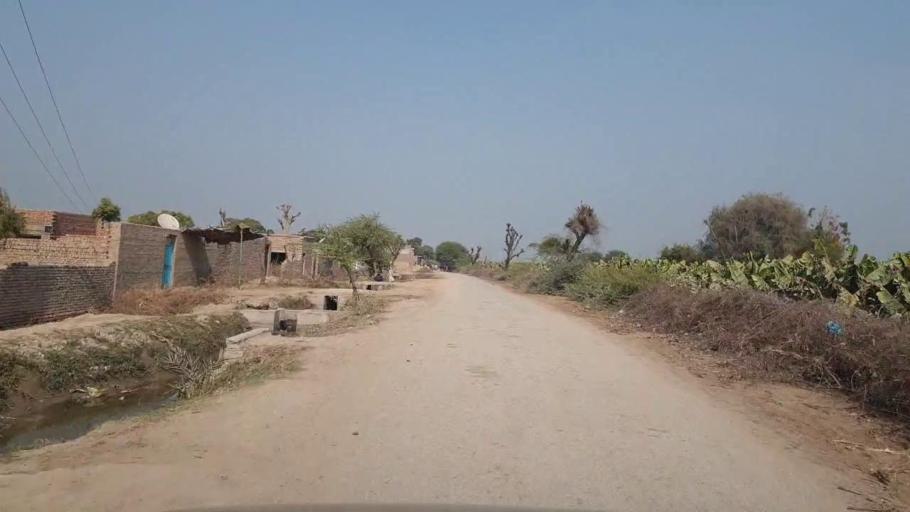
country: PK
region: Sindh
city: Bhit Shah
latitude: 25.7941
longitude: 68.4928
